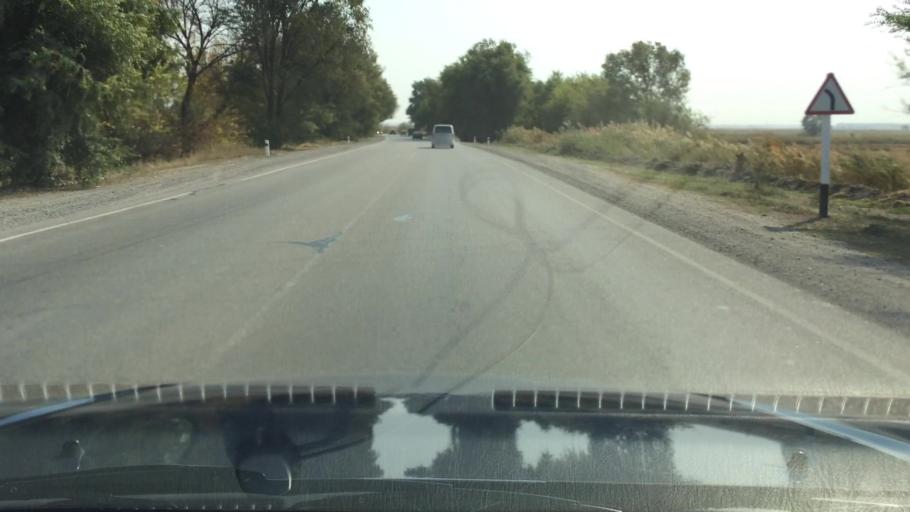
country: KG
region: Chuy
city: Lebedinovka
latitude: 42.9228
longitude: 74.7056
